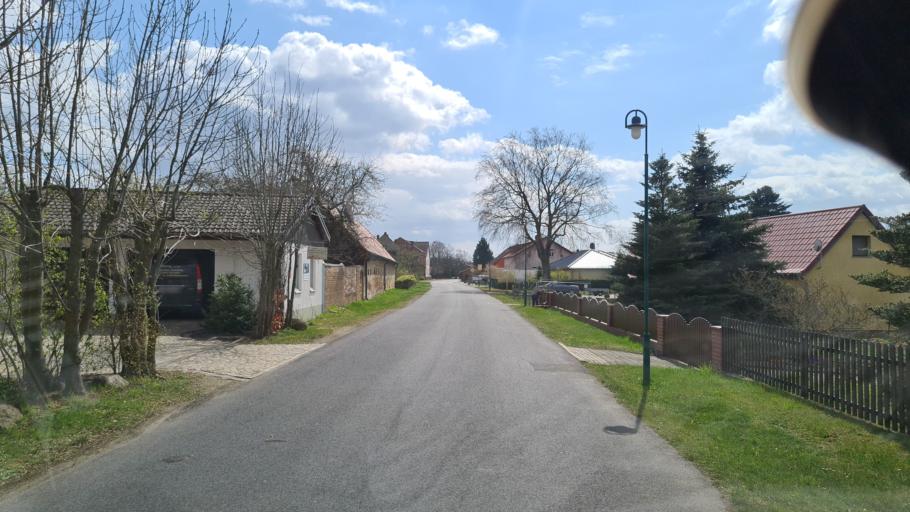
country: DE
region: Brandenburg
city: Senftenberg
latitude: 51.5082
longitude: 14.0695
